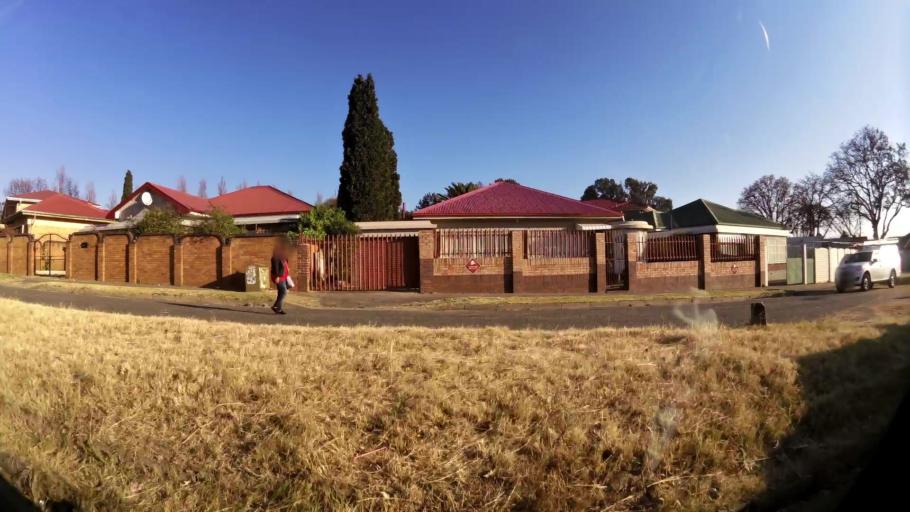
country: ZA
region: Gauteng
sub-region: City of Johannesburg Metropolitan Municipality
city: Johannesburg
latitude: -26.2396
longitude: 28.0256
